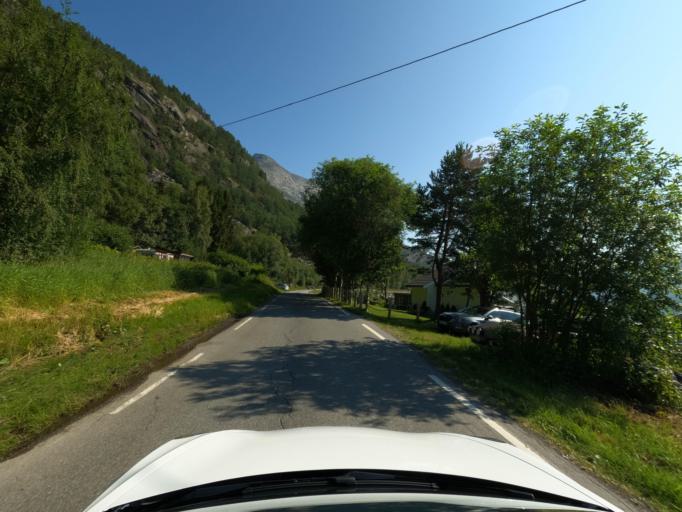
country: NO
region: Nordland
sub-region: Narvik
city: Narvik
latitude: 68.2801
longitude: 17.3836
